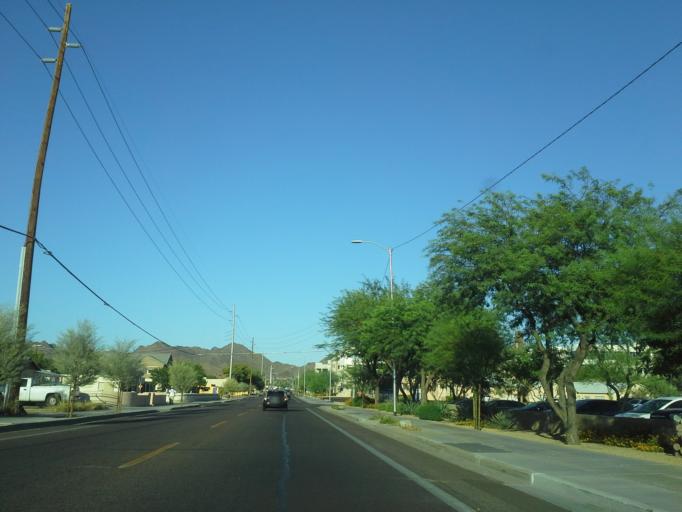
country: US
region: Arizona
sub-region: Maricopa County
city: Glendale
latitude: 33.5714
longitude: -112.0726
